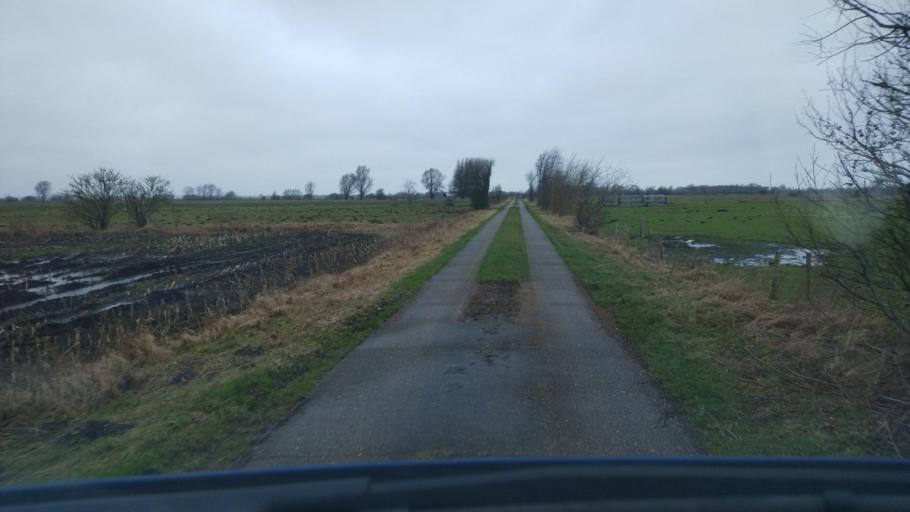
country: DE
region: Schleswig-Holstein
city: Gross Rheide
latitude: 54.4577
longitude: 9.4214
